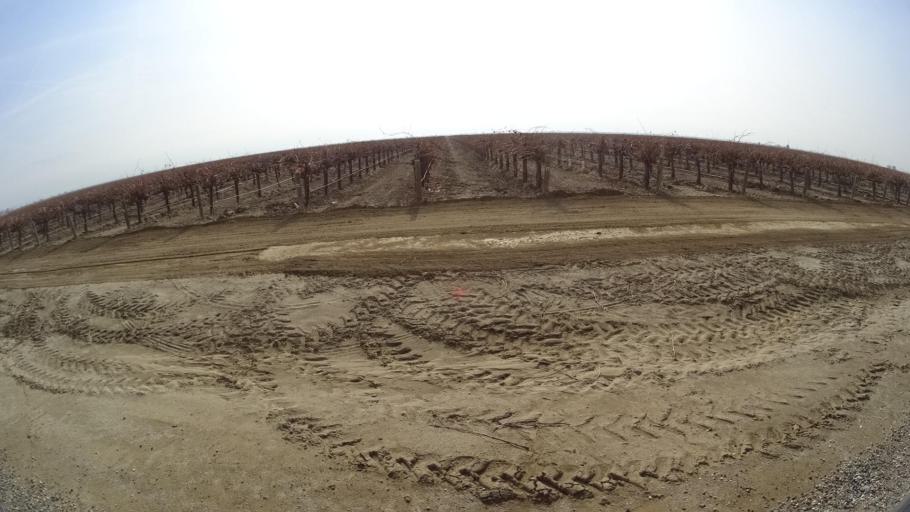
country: US
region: California
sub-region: Kern County
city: Arvin
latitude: 35.0453
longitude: -118.8575
